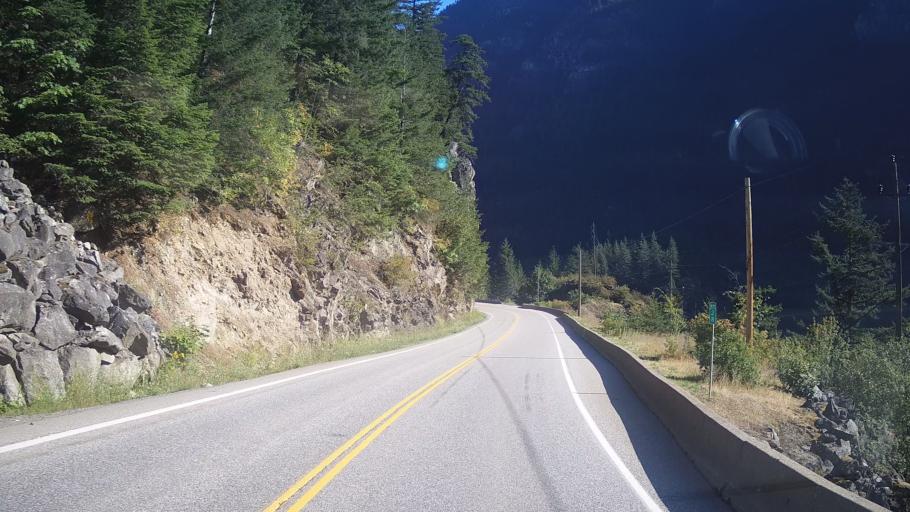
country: CA
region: British Columbia
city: Hope
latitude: 49.5781
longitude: -121.4029
